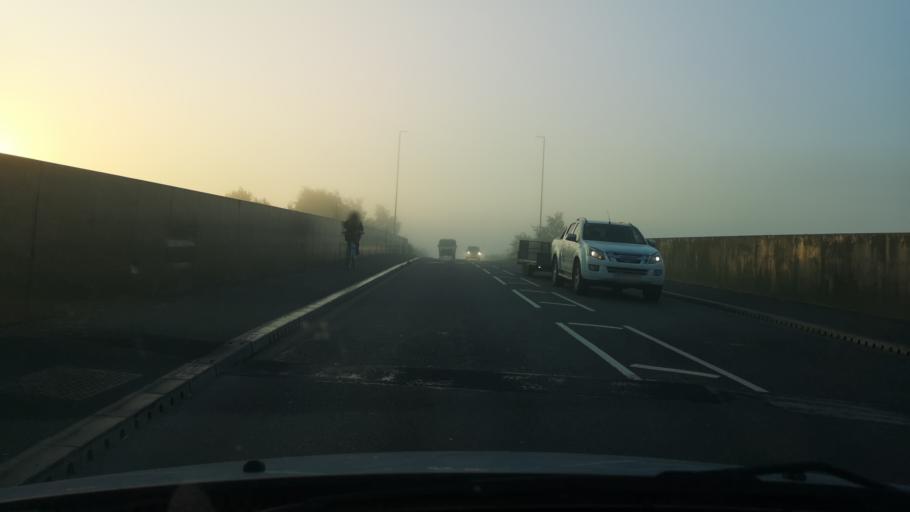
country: GB
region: England
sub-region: East Riding of Yorkshire
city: Airmyn
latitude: 53.7002
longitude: -0.8870
